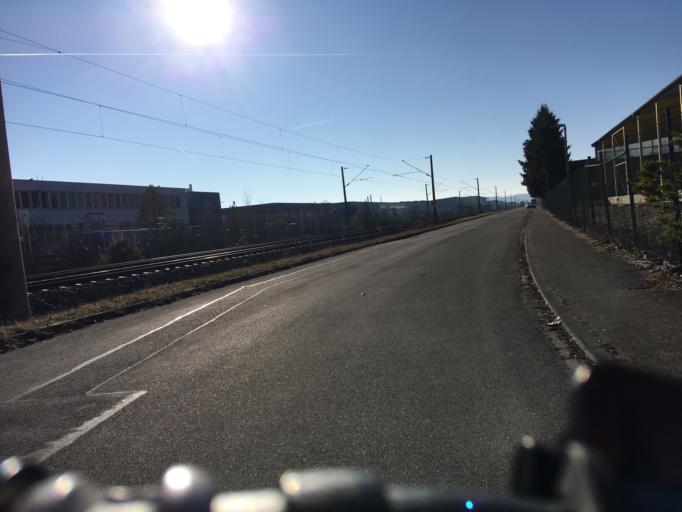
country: DE
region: Baden-Wuerttemberg
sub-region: Freiburg Region
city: Gottmadingen
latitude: 47.7415
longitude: 8.7956
